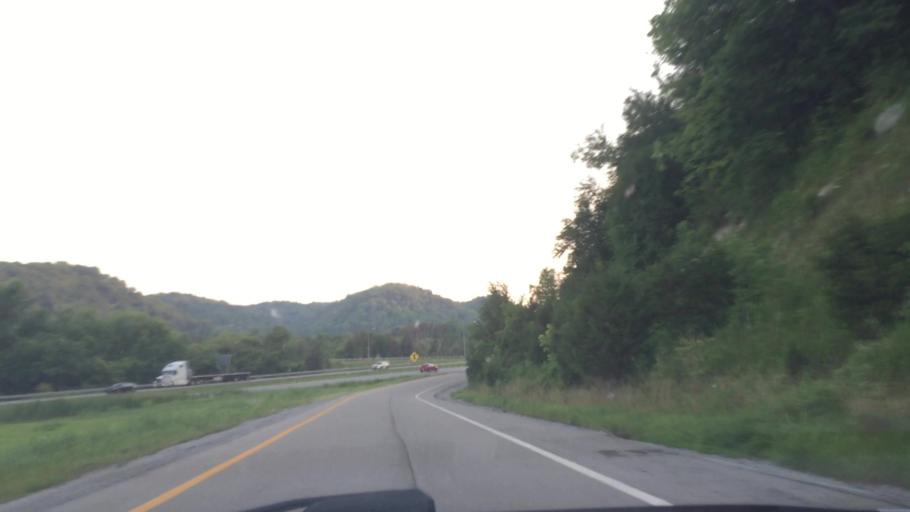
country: US
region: Kentucky
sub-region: Carroll County
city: Carrollton
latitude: 38.6316
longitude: -85.1411
